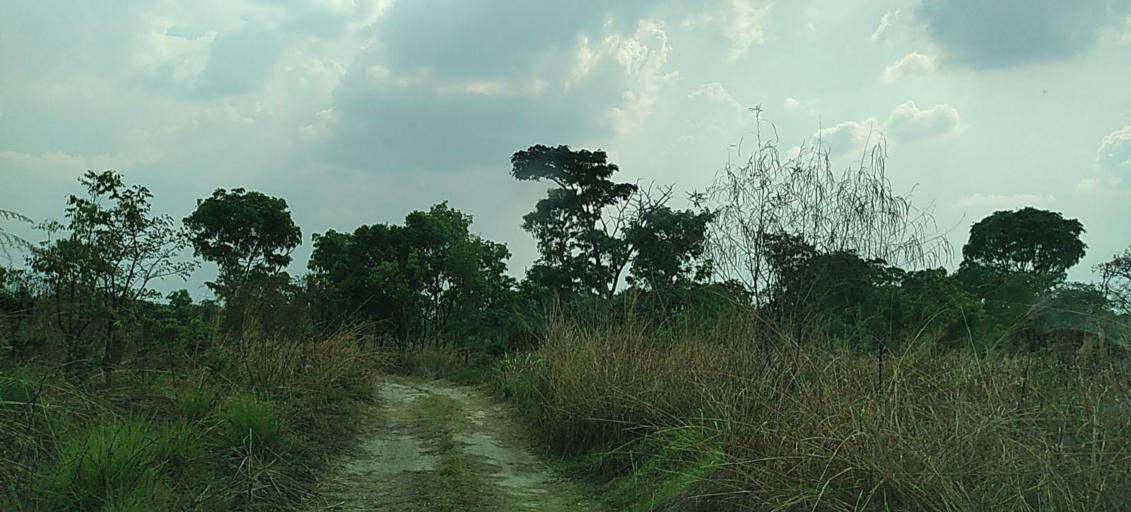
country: ZM
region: North-Western
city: Solwezi
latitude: -12.0950
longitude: 26.2846
